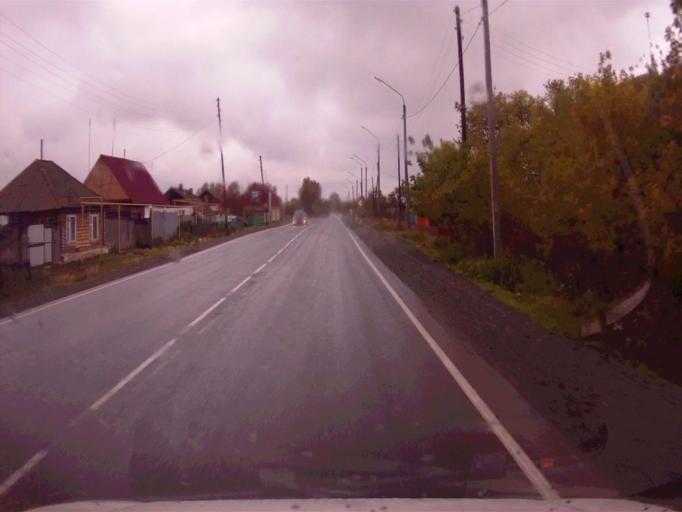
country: RU
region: Chelyabinsk
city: Tayginka
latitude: 55.4969
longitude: 60.6504
